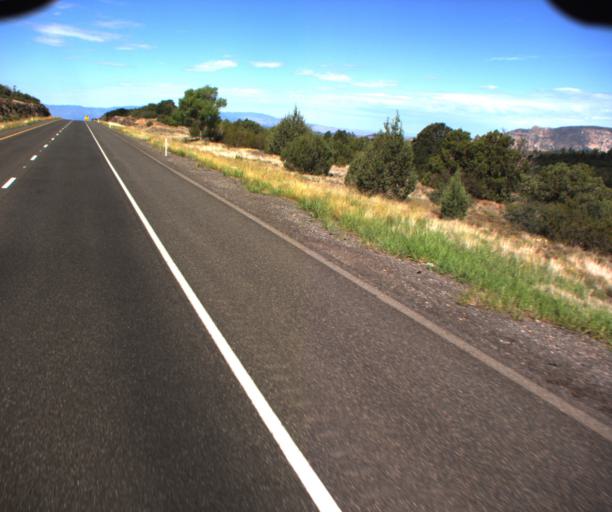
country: US
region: Arizona
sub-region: Yavapai County
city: Village of Oak Creek (Big Park)
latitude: 34.7786
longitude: -111.6277
